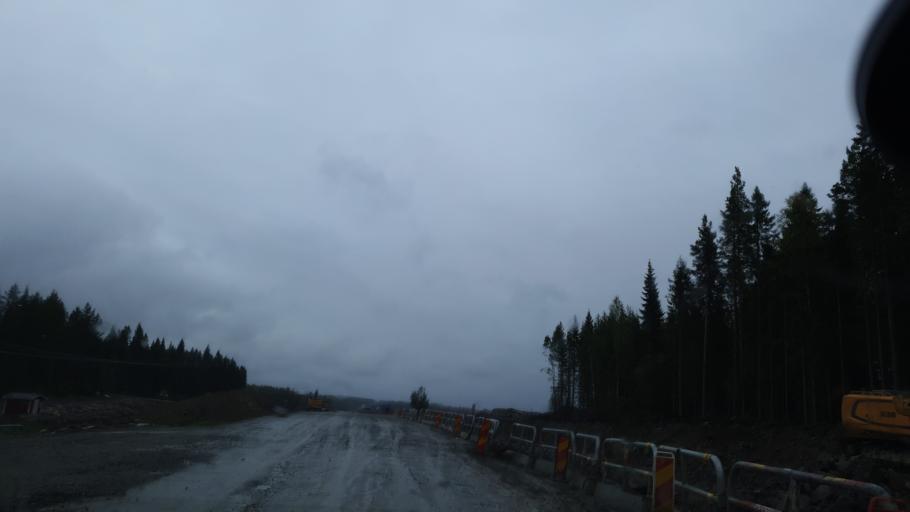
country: SE
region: Vaesterbotten
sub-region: Skelleftea Kommun
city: Soedra Bergsbyn
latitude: 64.7413
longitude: 21.0735
